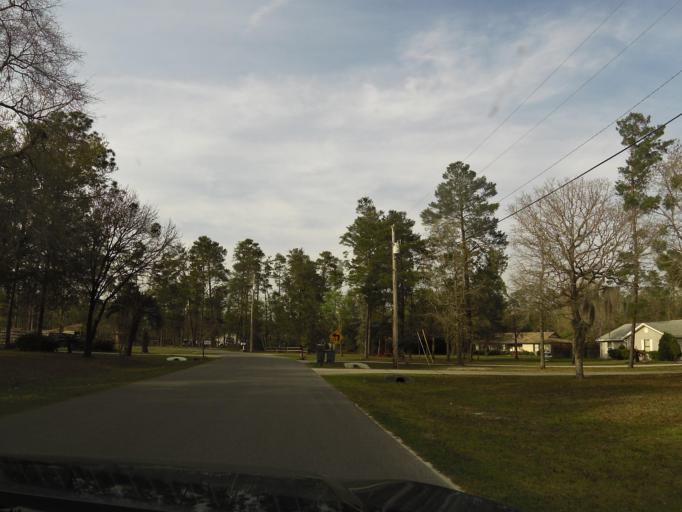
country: US
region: Florida
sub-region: Clay County
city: Middleburg
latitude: 30.1140
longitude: -81.8828
